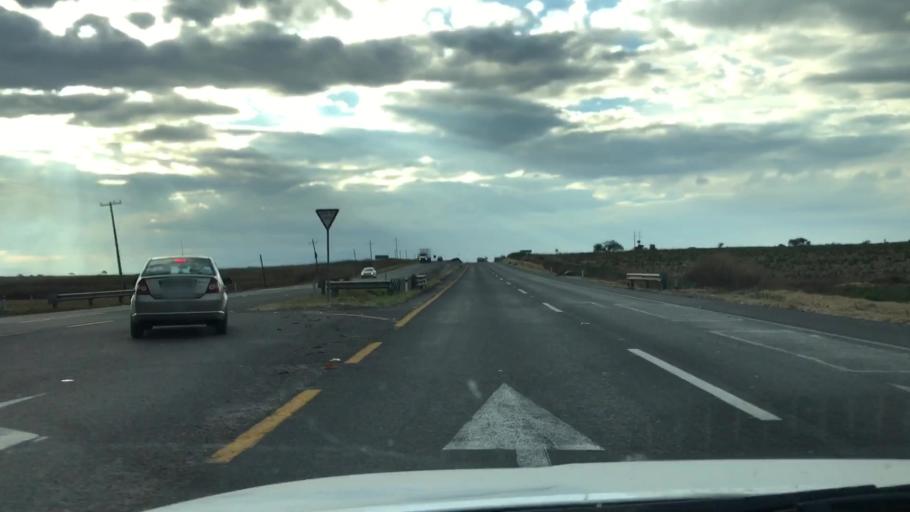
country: MX
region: Guanajuato
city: Penjamo
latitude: 20.3827
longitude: -101.8063
